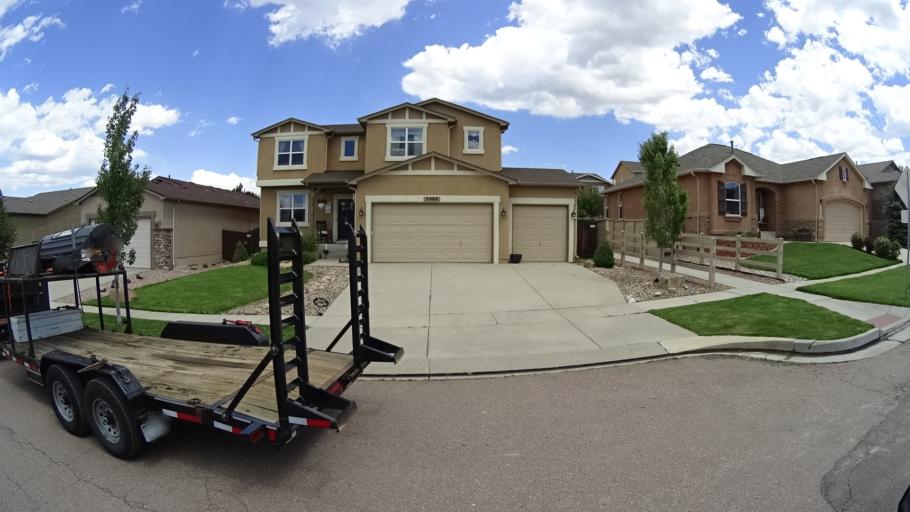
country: US
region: Colorado
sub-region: El Paso County
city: Black Forest
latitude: 38.9479
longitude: -104.7131
